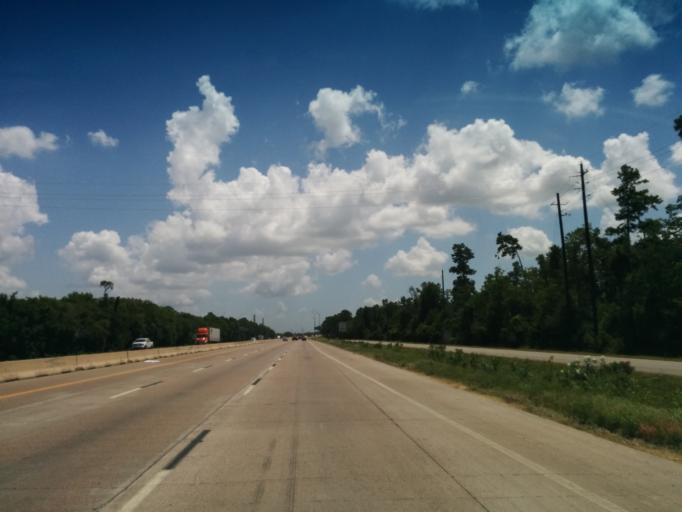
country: US
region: Texas
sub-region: Chambers County
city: Mont Belvieu
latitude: 29.8154
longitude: -94.9318
